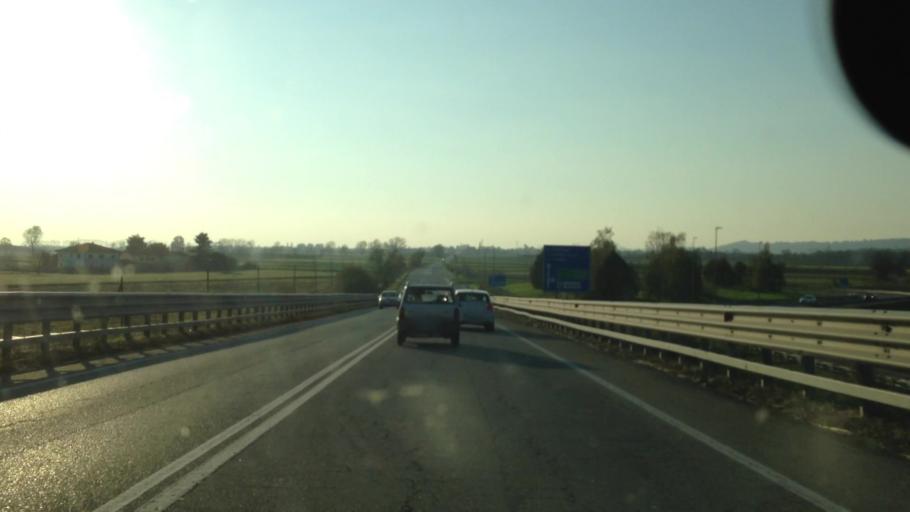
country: IT
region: Piedmont
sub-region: Provincia di Vercelli
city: Borgo d'Ale
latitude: 45.3200
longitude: 8.0698
